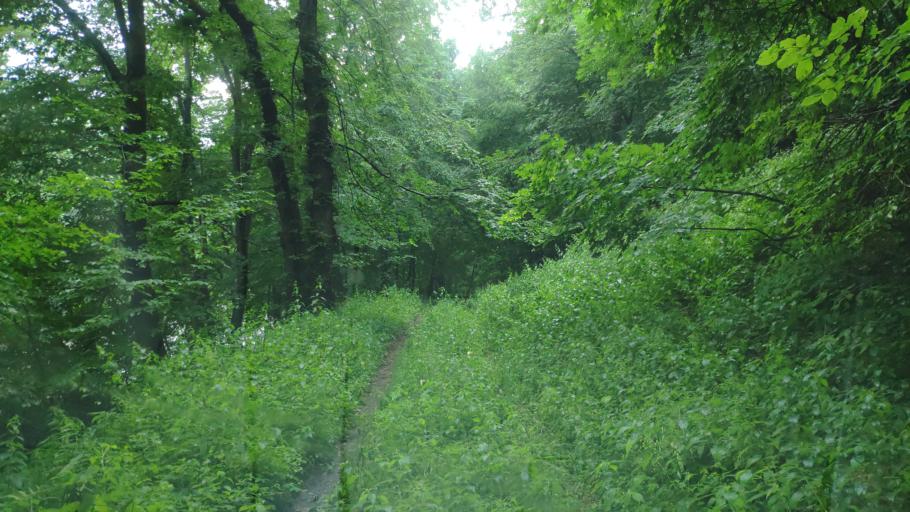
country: SK
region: Presovsky
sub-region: Okres Presov
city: Presov
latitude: 48.8671
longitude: 21.2059
